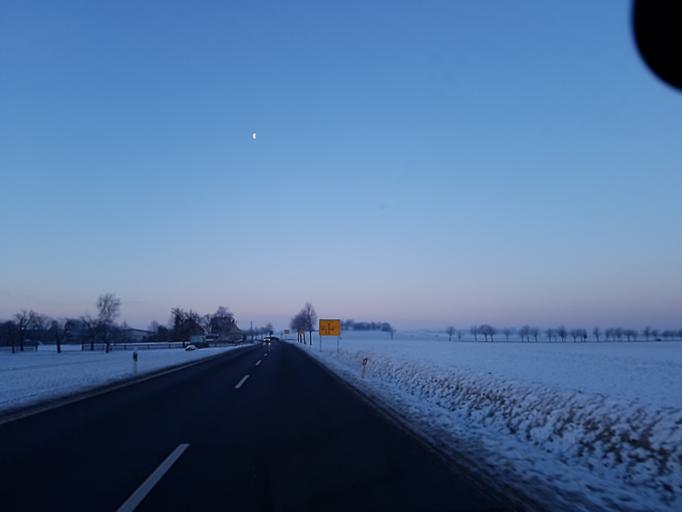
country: DE
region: Saxony
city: Oschatz
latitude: 51.3010
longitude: 13.1640
